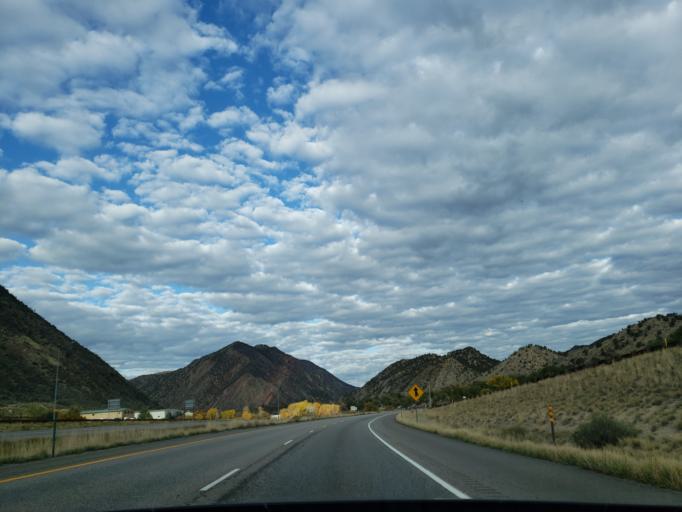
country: US
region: Colorado
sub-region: Garfield County
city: New Castle
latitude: 39.5663
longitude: -107.5182
